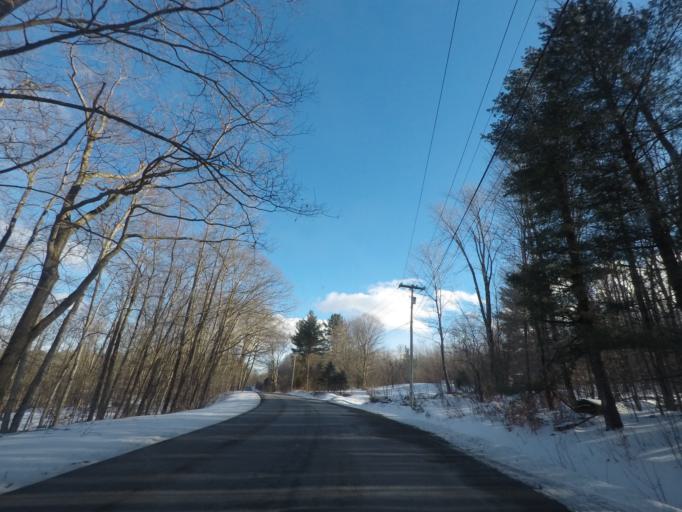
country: US
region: New York
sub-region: Rensselaer County
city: Hoosick Falls
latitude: 42.7907
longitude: -73.4010
